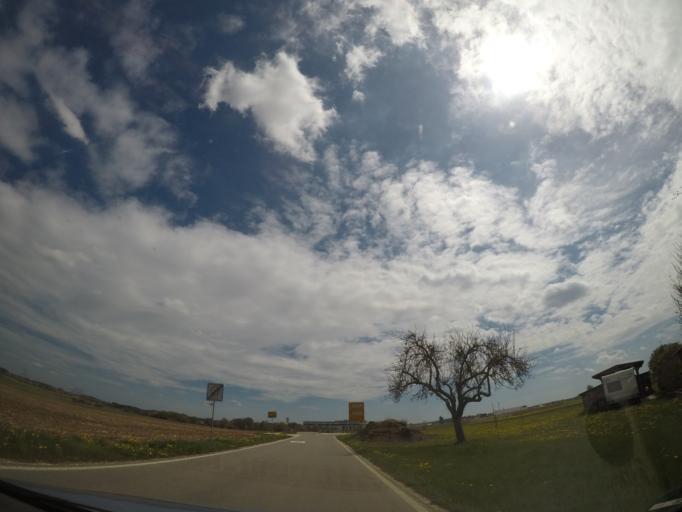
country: DE
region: Baden-Wuerttemberg
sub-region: Tuebingen Region
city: Berghulen
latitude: 48.4344
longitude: 9.7469
